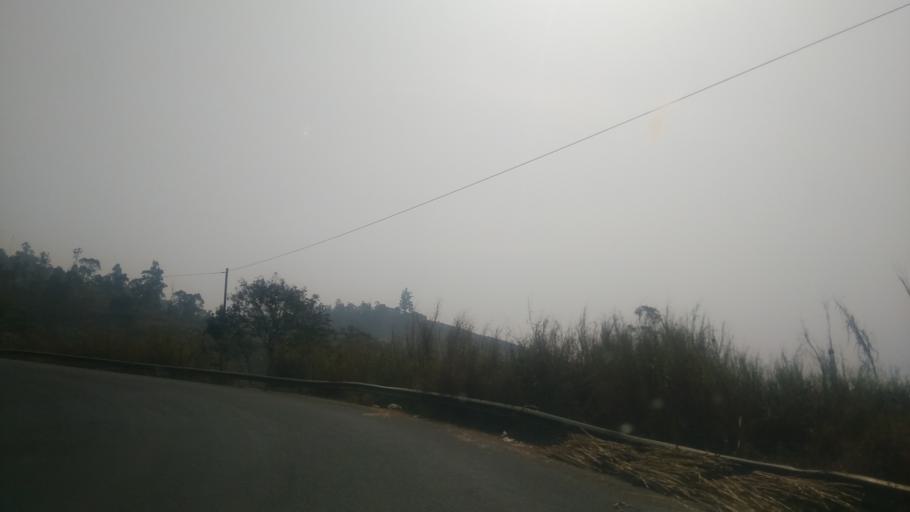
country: CM
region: West
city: Dschang
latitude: 5.4046
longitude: 10.0152
